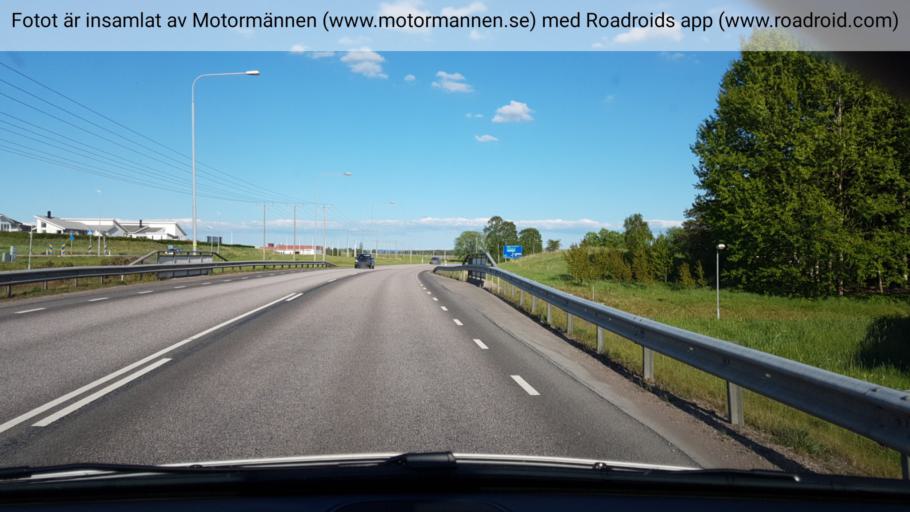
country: SE
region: Vaestra Goetaland
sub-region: Skara Kommun
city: Skara
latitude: 58.3938
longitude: 13.4546
